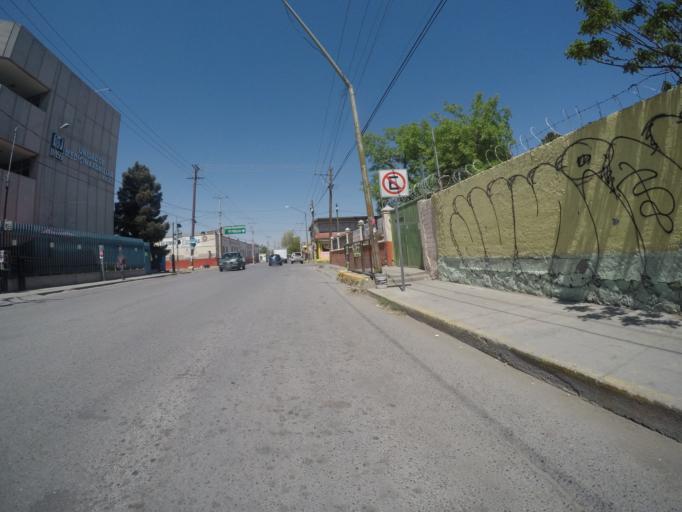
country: MX
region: Chihuahua
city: Ciudad Juarez
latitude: 31.7249
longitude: -106.4794
